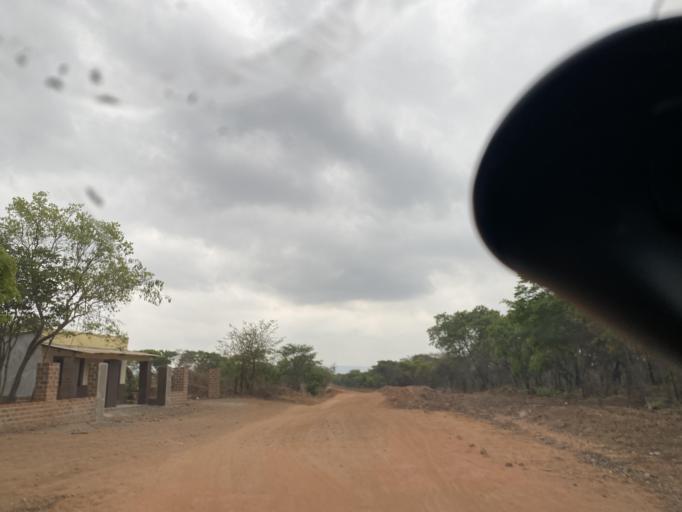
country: ZM
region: Lusaka
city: Chongwe
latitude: -15.2697
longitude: 28.7317
